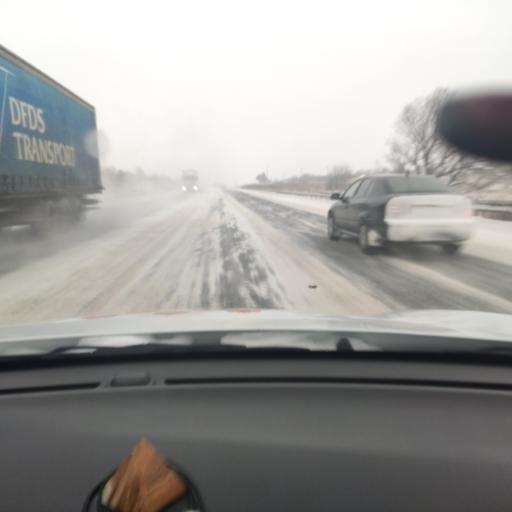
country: RU
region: Tatarstan
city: Verkhniy Uslon
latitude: 55.7213
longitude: 48.8338
